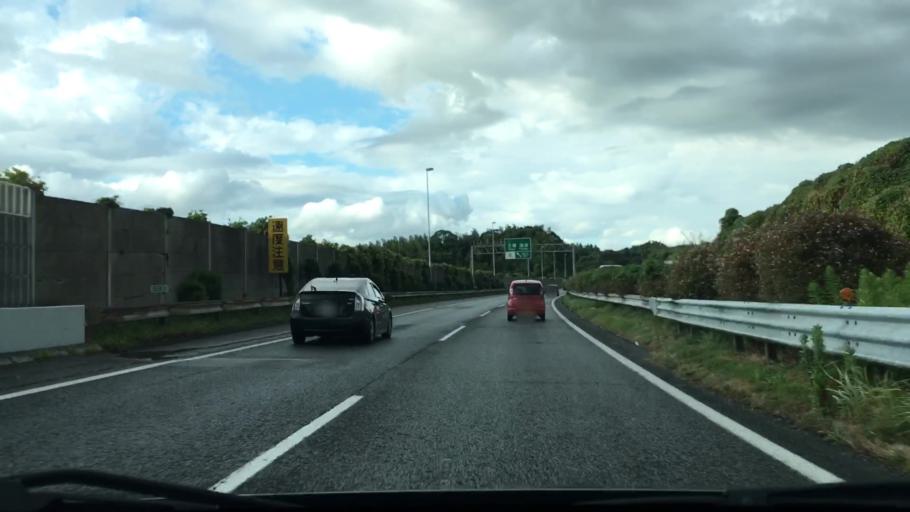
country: JP
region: Fukuoka
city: Koga
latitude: 33.7149
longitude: 130.4906
